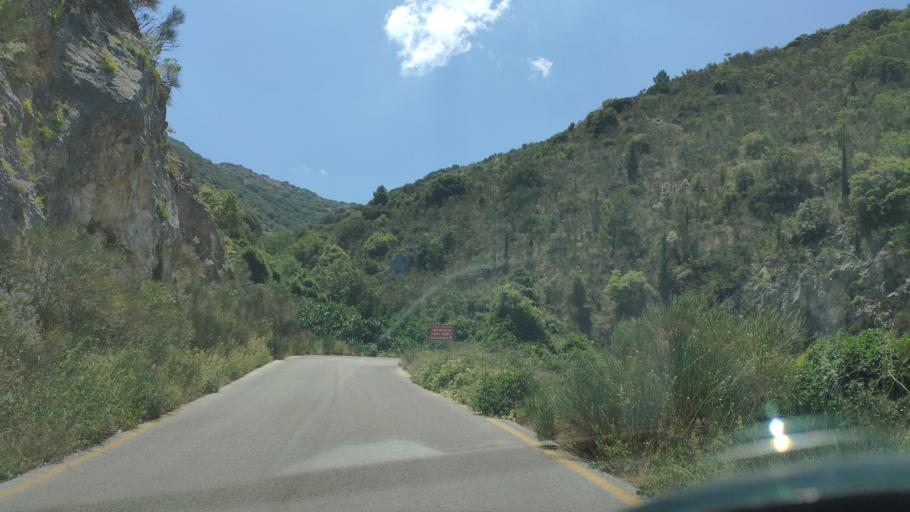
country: GR
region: Ionian Islands
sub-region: Lefkada
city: Nidri
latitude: 38.7442
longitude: 20.6216
